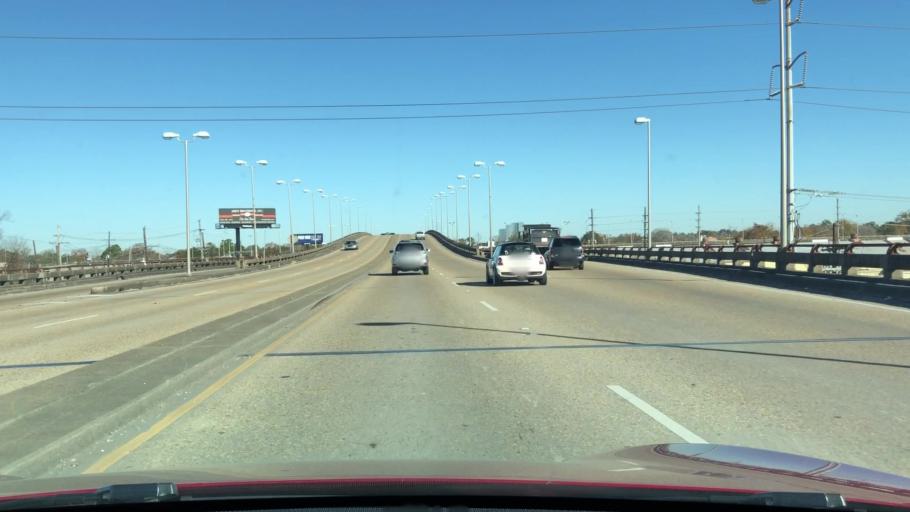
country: US
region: Louisiana
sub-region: Jefferson Parish
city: Jefferson
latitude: 29.9720
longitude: -90.1564
